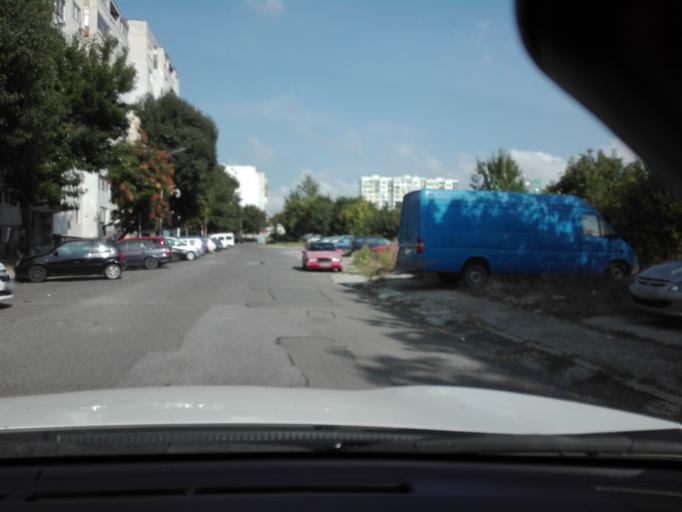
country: BG
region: Burgas
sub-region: Obshtina Burgas
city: Burgas
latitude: 42.4532
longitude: 27.4242
